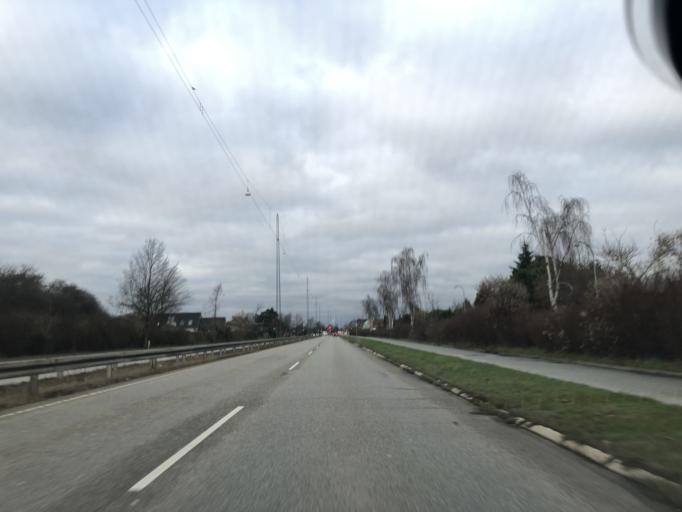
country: DK
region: Capital Region
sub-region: Hvidovre Kommune
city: Hvidovre
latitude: 55.6320
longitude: 12.4692
